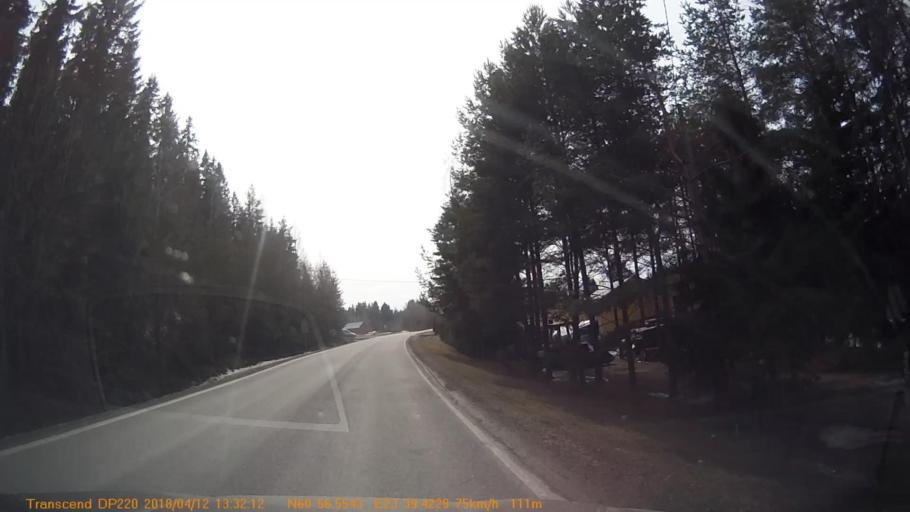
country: FI
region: Haeme
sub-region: Forssa
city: Forssa
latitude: 60.9425
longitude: 23.6570
